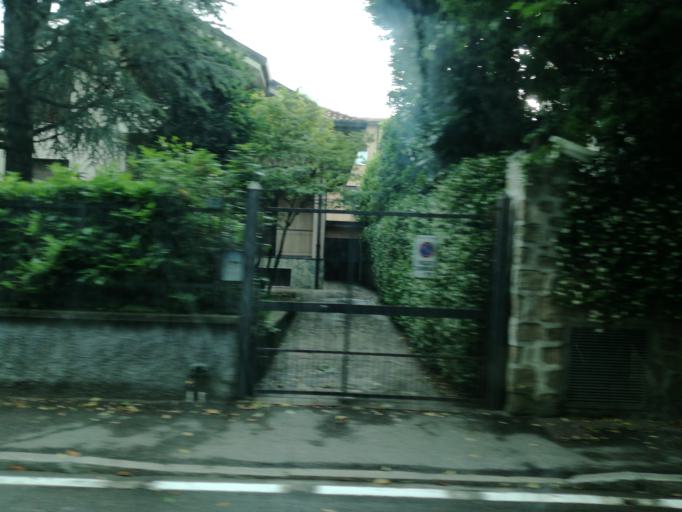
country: IT
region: Lombardy
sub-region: Provincia di Monza e Brianza
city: Velasca
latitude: 45.6185
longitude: 9.3506
